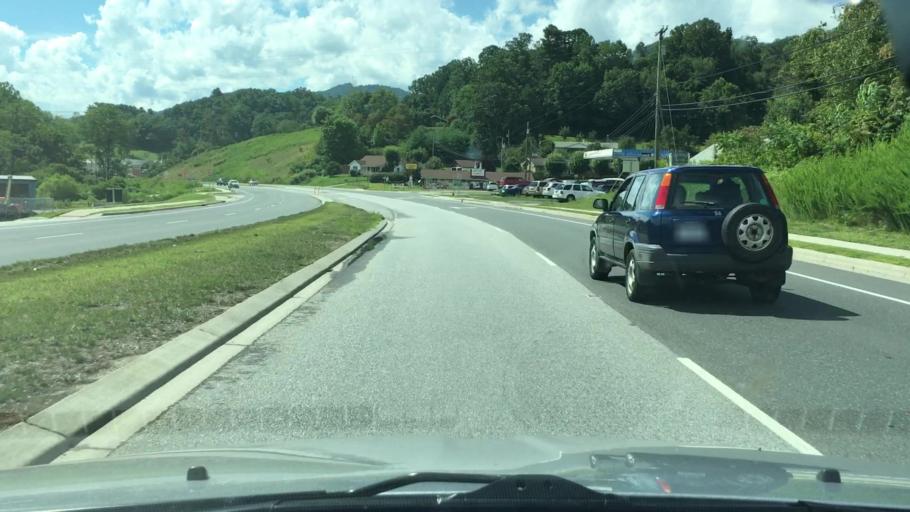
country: US
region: North Carolina
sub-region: Yancey County
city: Burnsville
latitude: 35.9175
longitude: -82.2718
